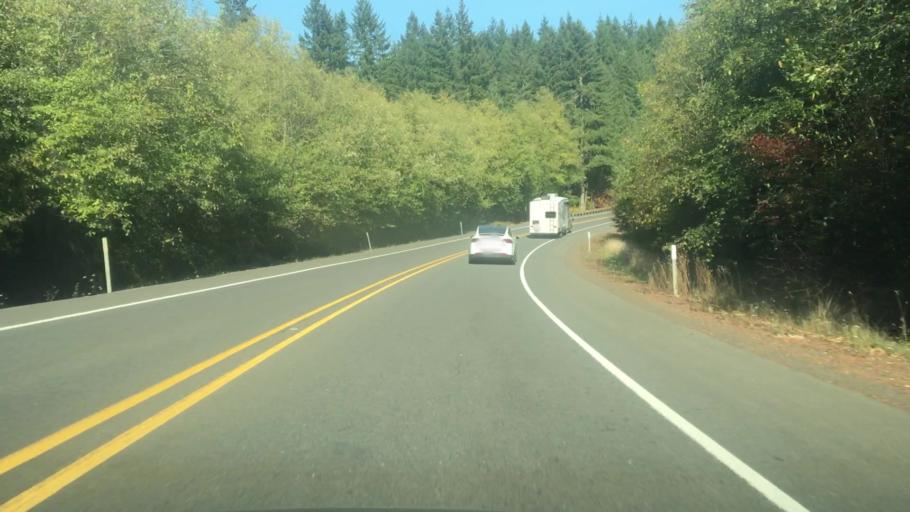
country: US
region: Oregon
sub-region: Polk County
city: Grand Ronde
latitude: 45.0680
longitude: -123.7288
